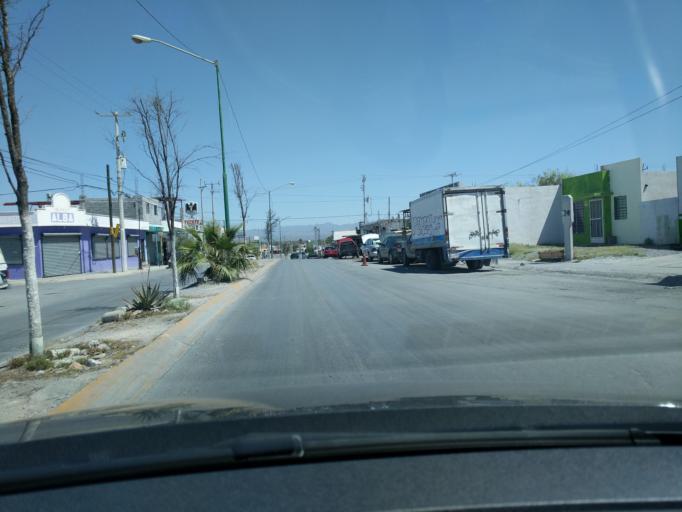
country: MX
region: Nuevo Leon
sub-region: Pesqueria
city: Colinas del Aeropuerto
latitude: 25.8184
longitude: -100.1076
